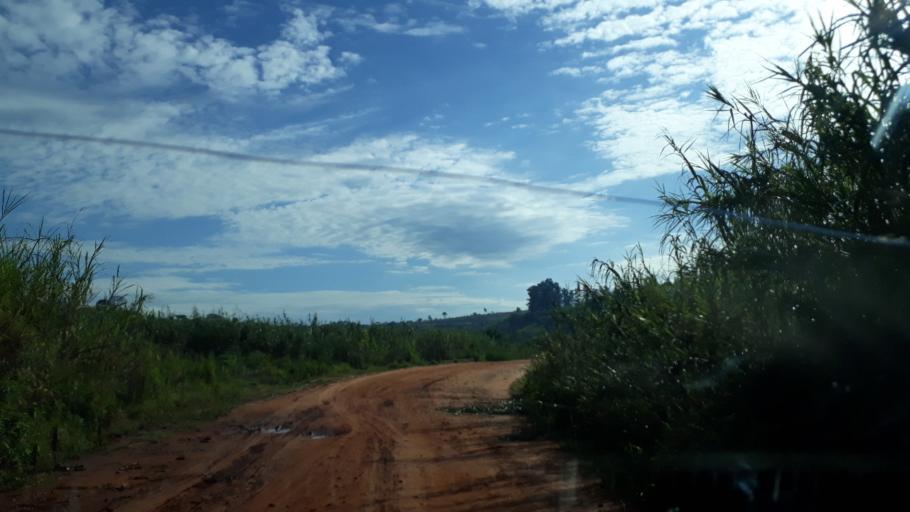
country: UG
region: Northern Region
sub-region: Zombo District
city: Paidha
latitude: 2.2615
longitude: 30.9391
